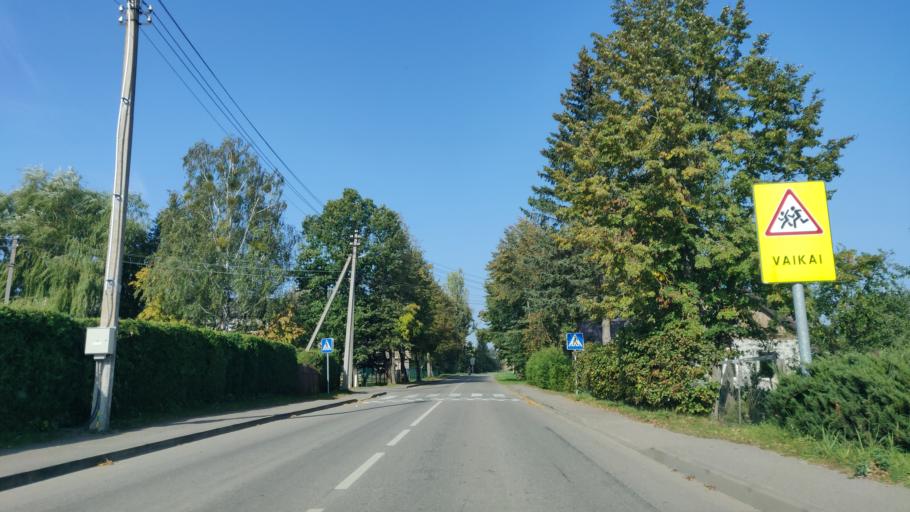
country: LT
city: Sirvintos
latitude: 54.9509
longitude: 24.8392
